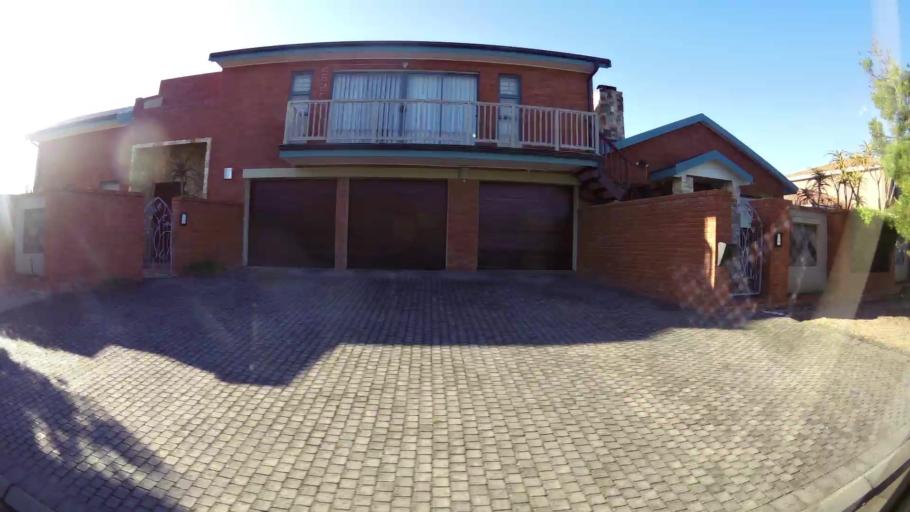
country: ZA
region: Western Cape
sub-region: Eden District Municipality
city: George
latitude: -33.9579
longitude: 22.4447
